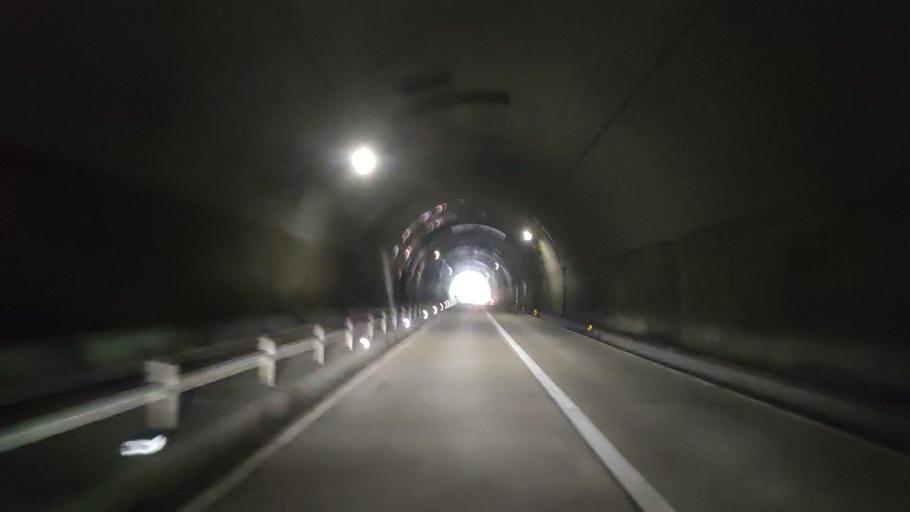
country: JP
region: Wakayama
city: Shingu
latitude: 33.8174
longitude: 135.7588
